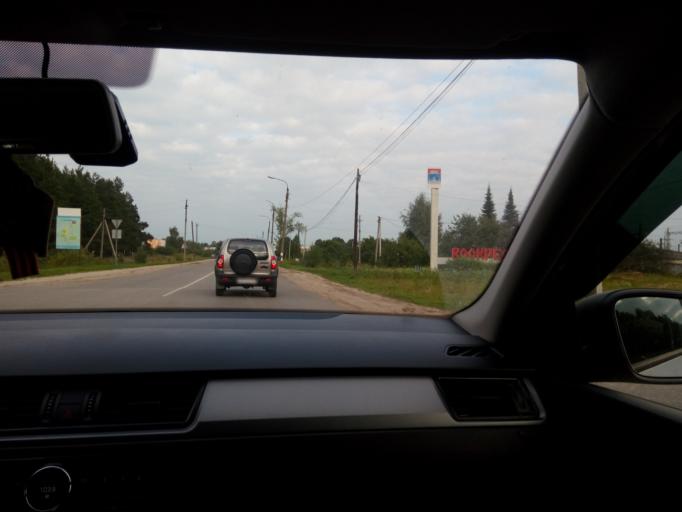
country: RU
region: Nizjnij Novgorod
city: Voskresenskoye
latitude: 56.8391
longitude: 45.4203
